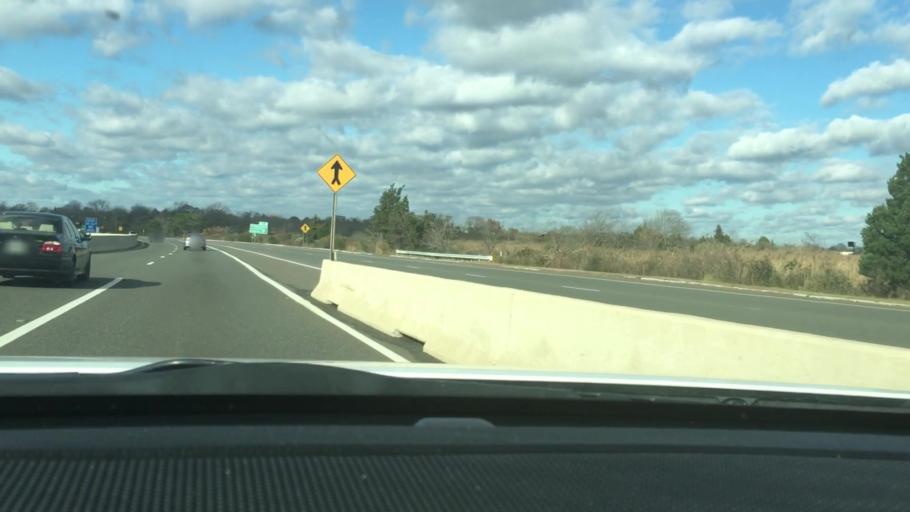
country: US
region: New Jersey
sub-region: Atlantic County
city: Pleasantville
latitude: 39.3925
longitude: -74.5106
